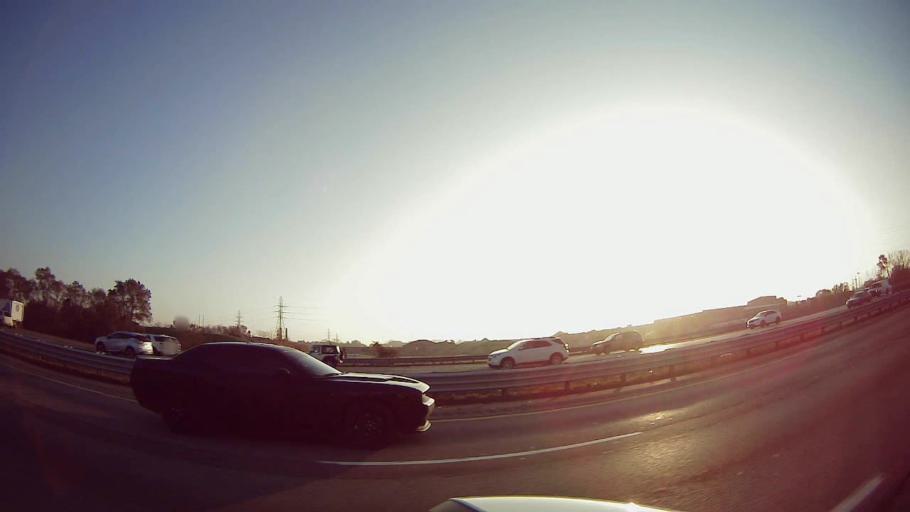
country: US
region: Michigan
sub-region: Oakland County
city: Madison Heights
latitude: 42.5079
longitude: -83.1152
